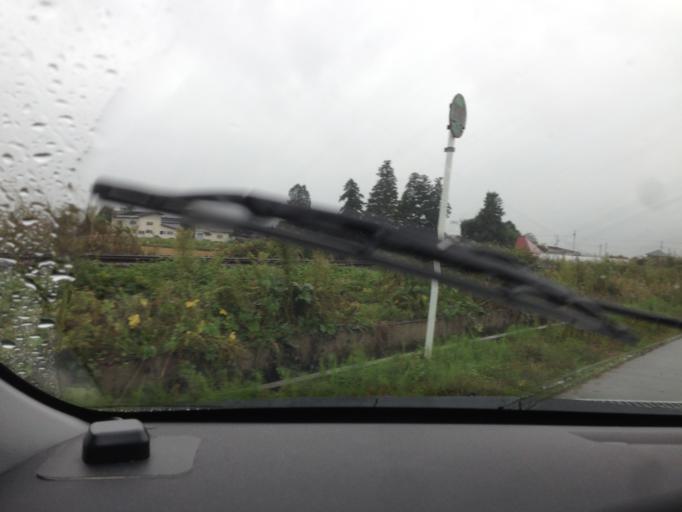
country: JP
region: Fukushima
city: Kitakata
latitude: 37.4628
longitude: 139.8755
